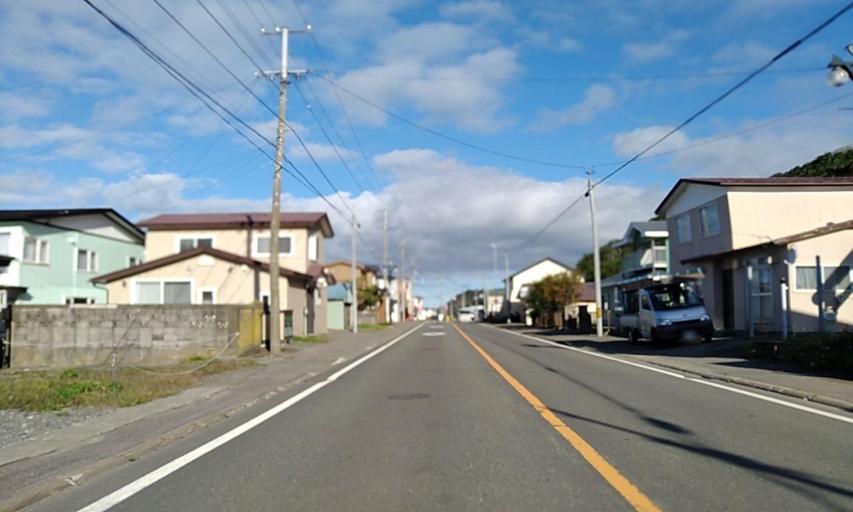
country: JP
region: Hokkaido
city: Shizunai-furukawacho
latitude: 42.1978
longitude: 142.6634
